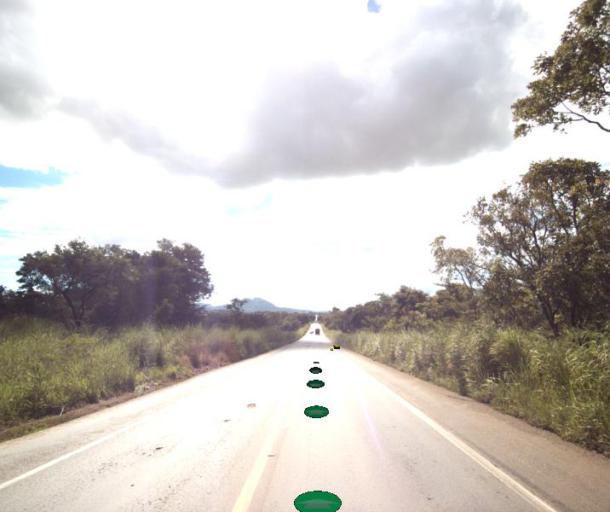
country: BR
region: Goias
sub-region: Jaragua
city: Jaragua
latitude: -15.8820
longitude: -49.2455
